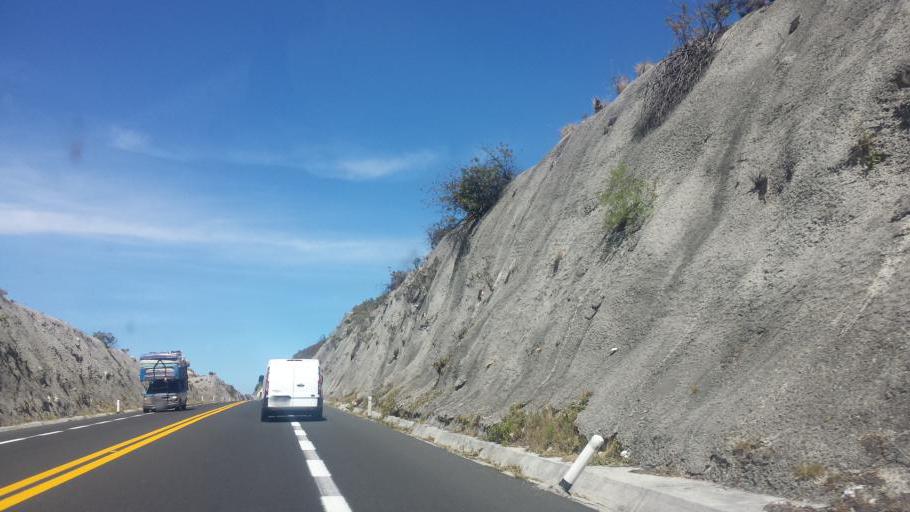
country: MX
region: Puebla
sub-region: San Jose Miahuatlan
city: San Pedro Tetitlan
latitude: 17.9993
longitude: -97.3549
